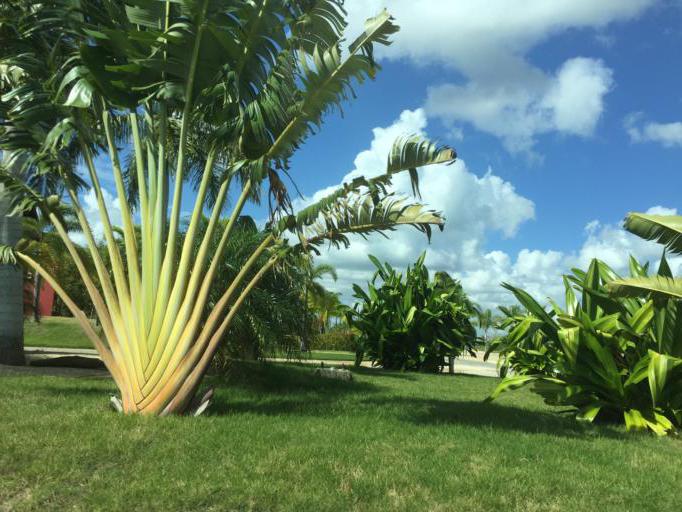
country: DO
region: Santo Domingo
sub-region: Santo Domingo
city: Boca Chica
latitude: 18.4679
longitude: -69.6536
